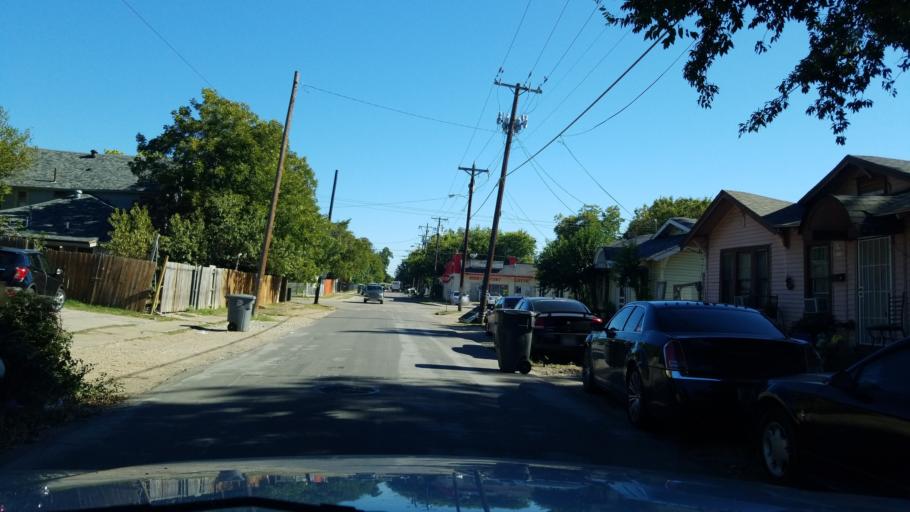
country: US
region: Texas
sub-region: Dallas County
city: Highland Park
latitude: 32.7952
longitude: -96.7533
